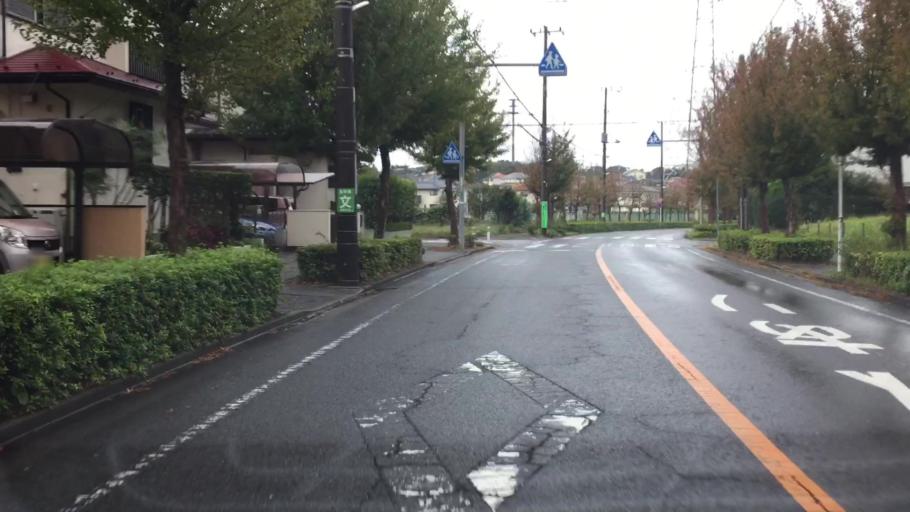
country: JP
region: Ibaraki
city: Toride
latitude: 35.8578
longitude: 140.1185
